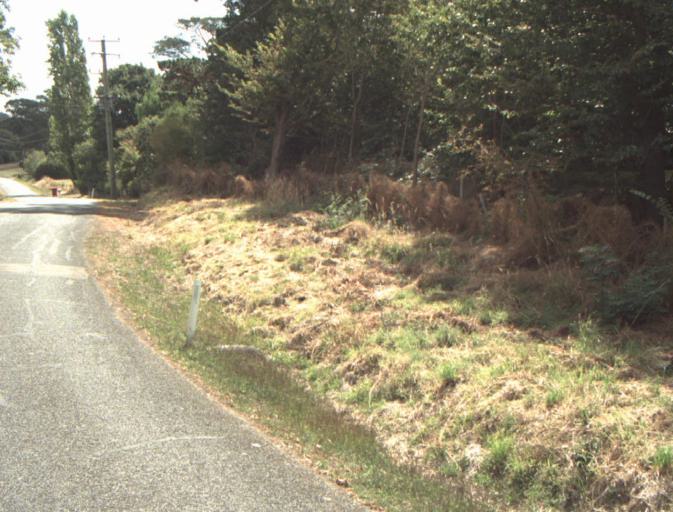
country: AU
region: Tasmania
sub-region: Launceston
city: Mayfield
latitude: -41.3159
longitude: 147.0046
